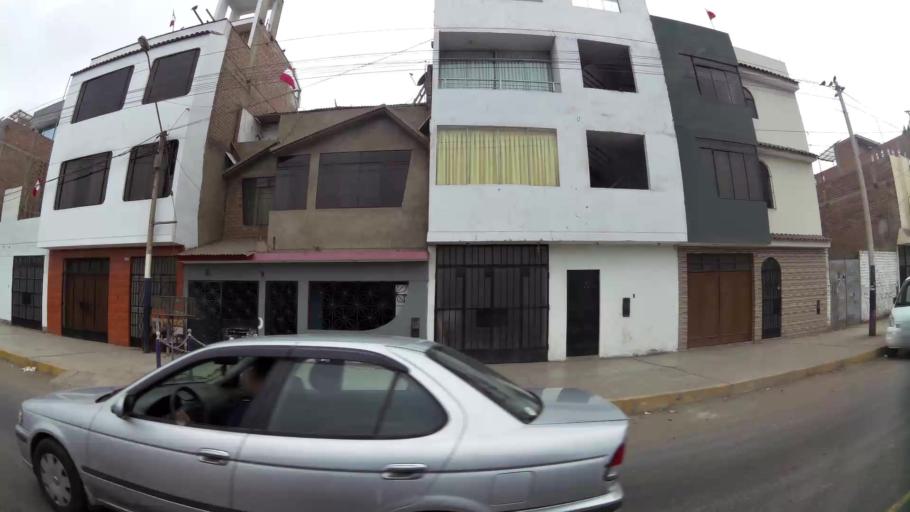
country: PE
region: Lima
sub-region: Lima
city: Surco
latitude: -12.1829
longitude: -77.0140
